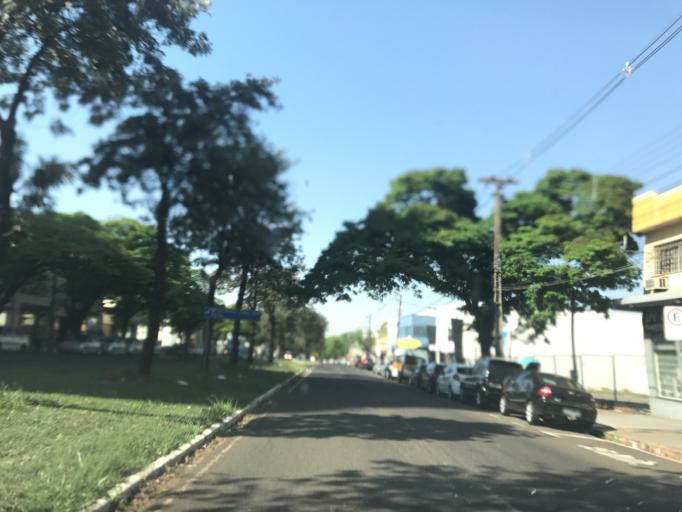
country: BR
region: Parana
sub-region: Maringa
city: Maringa
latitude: -23.4433
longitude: -51.9328
